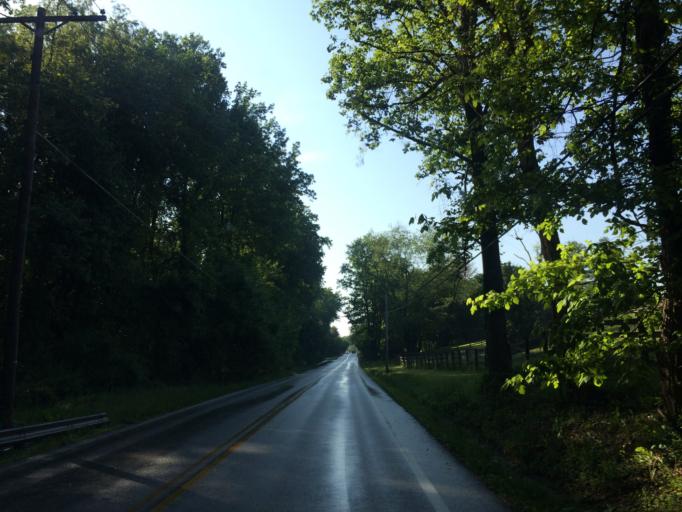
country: US
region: Maryland
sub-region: Howard County
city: Highland
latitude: 39.2585
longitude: -76.9692
